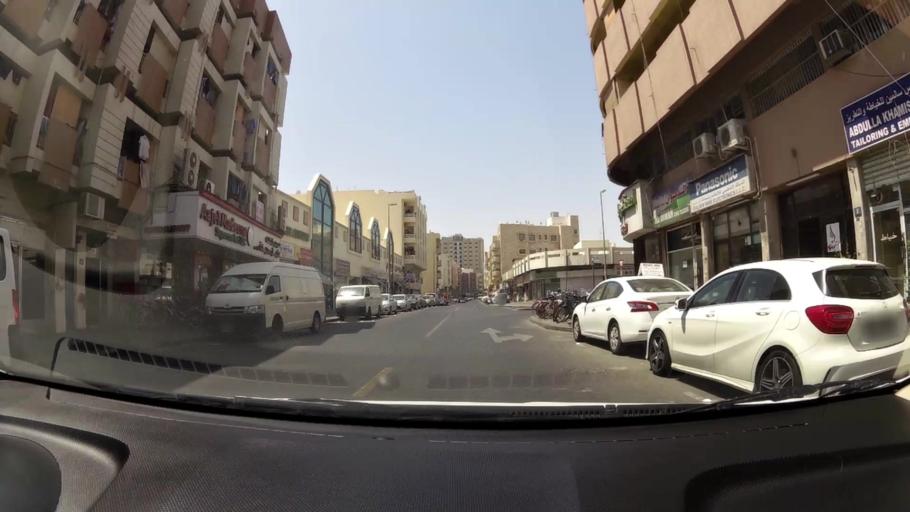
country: AE
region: Ash Shariqah
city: Sharjah
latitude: 25.2747
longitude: 55.3133
